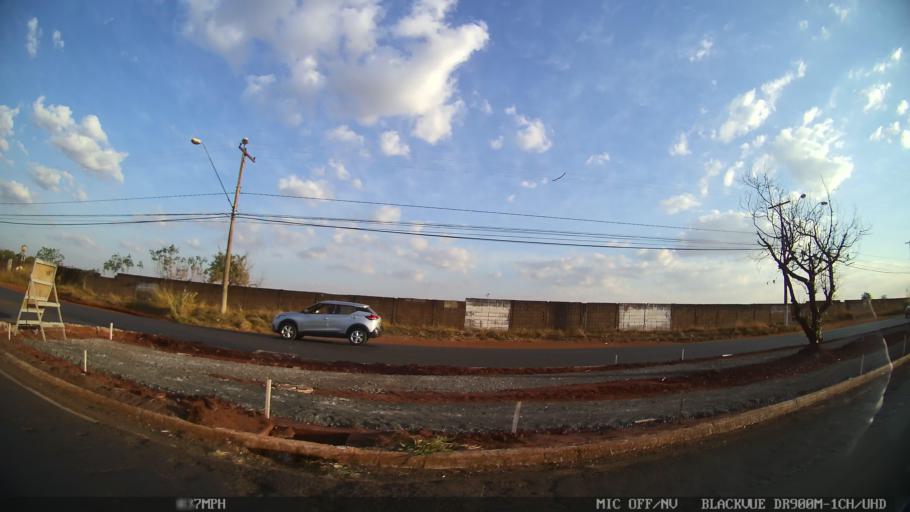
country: BR
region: Sao Paulo
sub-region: Ribeirao Preto
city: Ribeirao Preto
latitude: -21.1474
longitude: -47.7644
